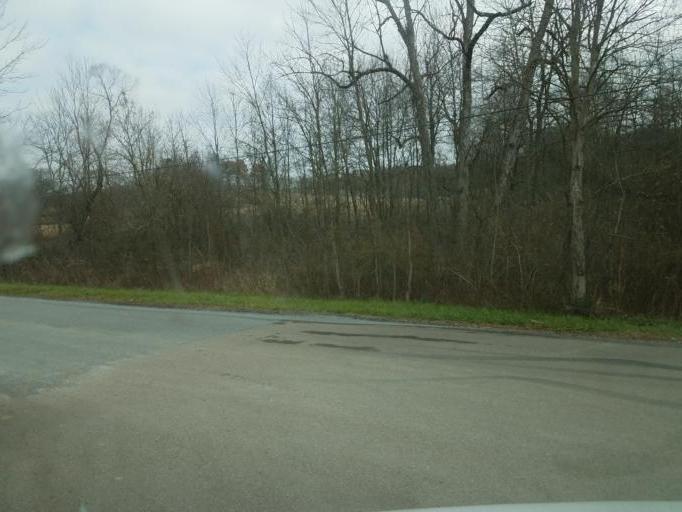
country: US
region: Ohio
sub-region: Knox County
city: Danville
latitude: 40.5086
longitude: -82.2866
